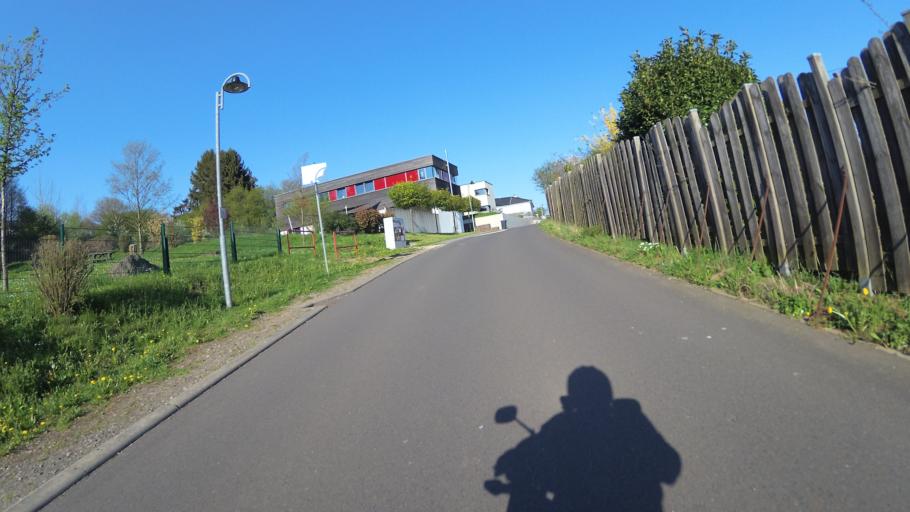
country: DE
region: Saarland
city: Illingen
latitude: 49.3734
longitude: 7.0707
